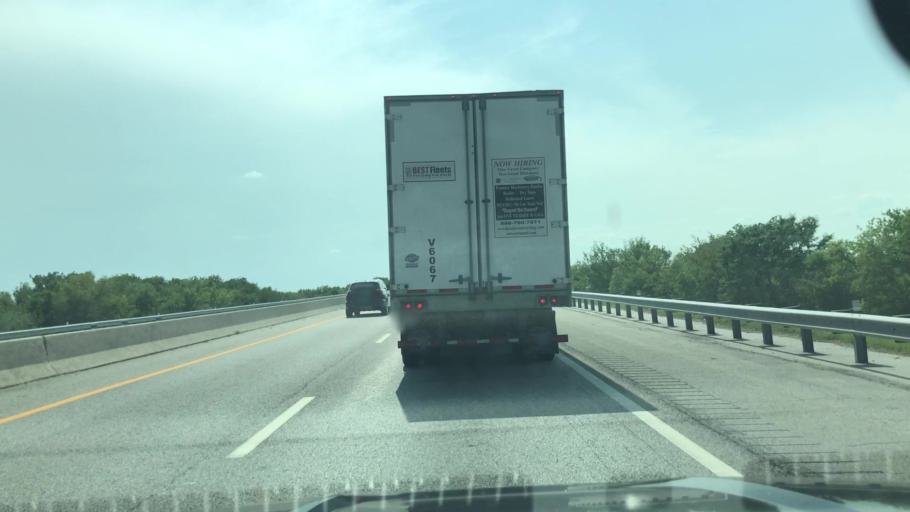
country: US
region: Oklahoma
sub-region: Ottawa County
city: Afton
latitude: 36.7180
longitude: -94.9477
